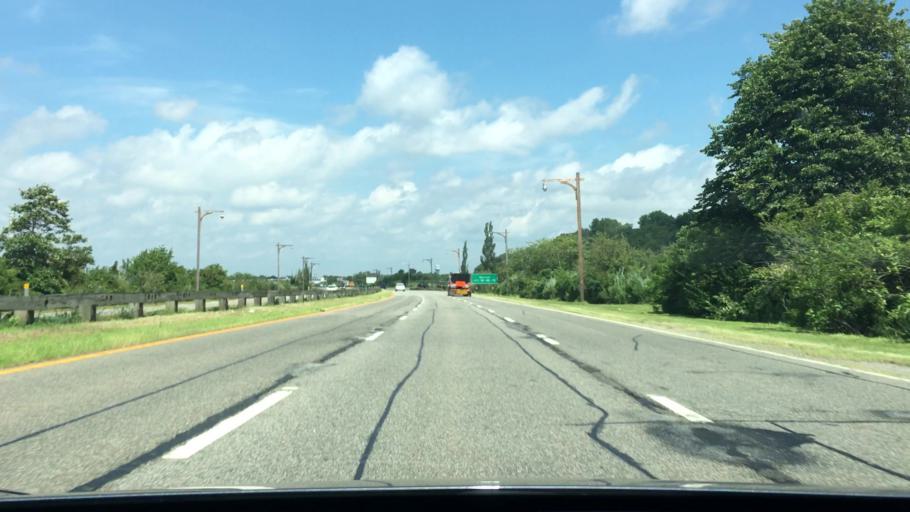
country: US
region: New York
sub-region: Nassau County
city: Merrick
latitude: 40.6390
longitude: -73.5624
